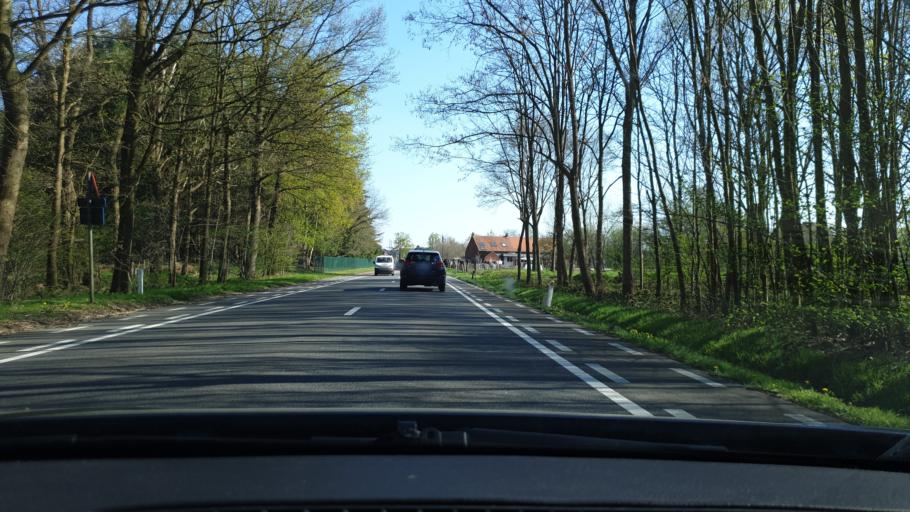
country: BE
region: Flanders
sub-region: Provincie Antwerpen
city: Laakdal
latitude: 51.0731
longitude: 5.0363
